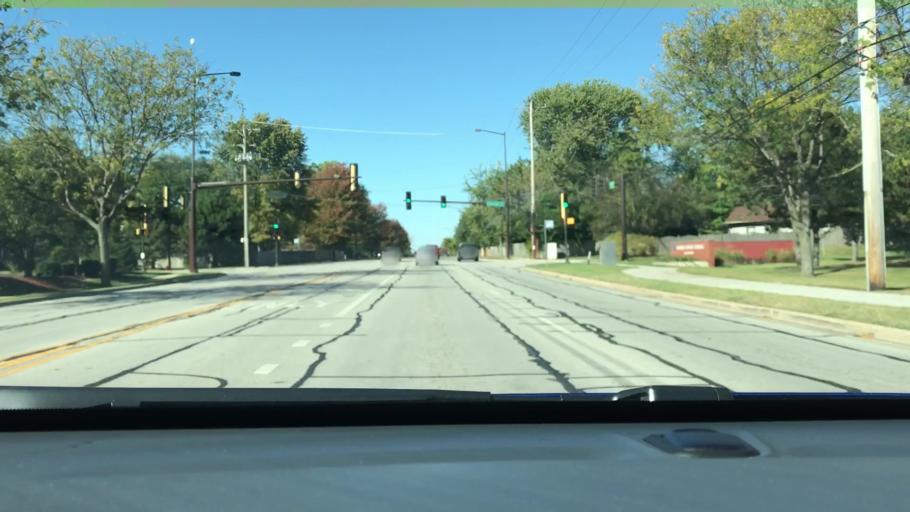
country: US
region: Illinois
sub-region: Kane County
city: North Aurora
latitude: 41.7811
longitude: -88.3586
